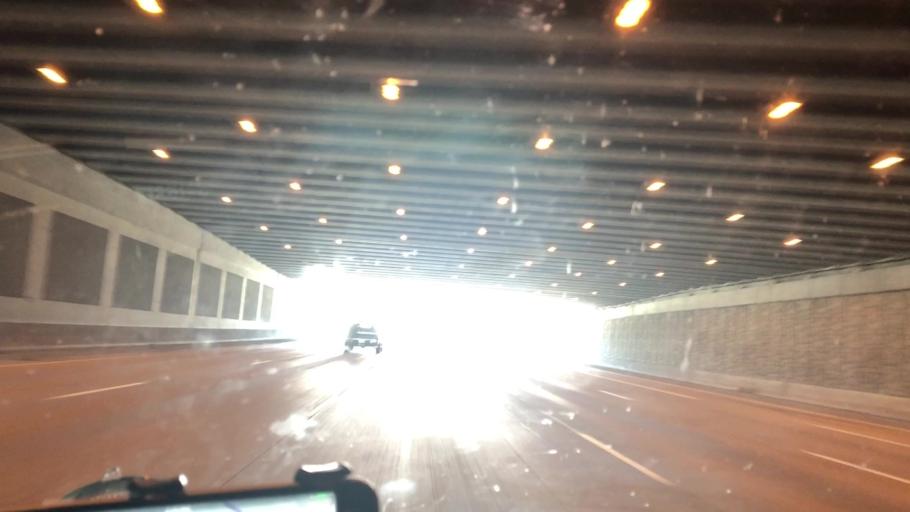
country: US
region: Idaho
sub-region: Ada County
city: Garden City
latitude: 43.5903
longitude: -116.2746
